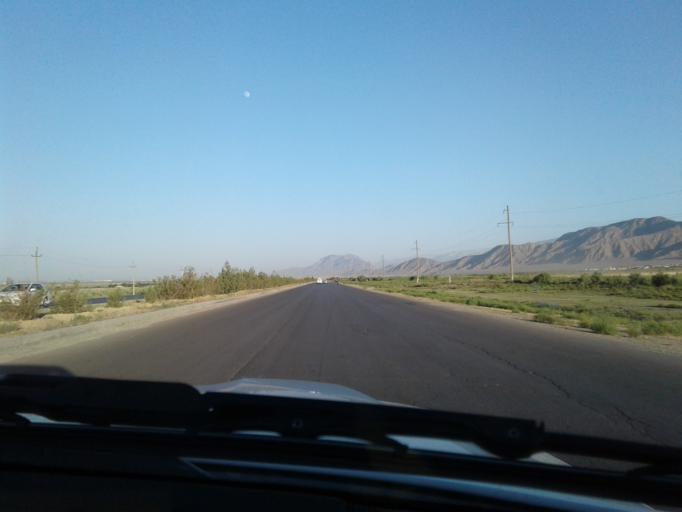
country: TM
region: Ahal
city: Arcabil
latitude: 38.2132
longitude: 57.8102
